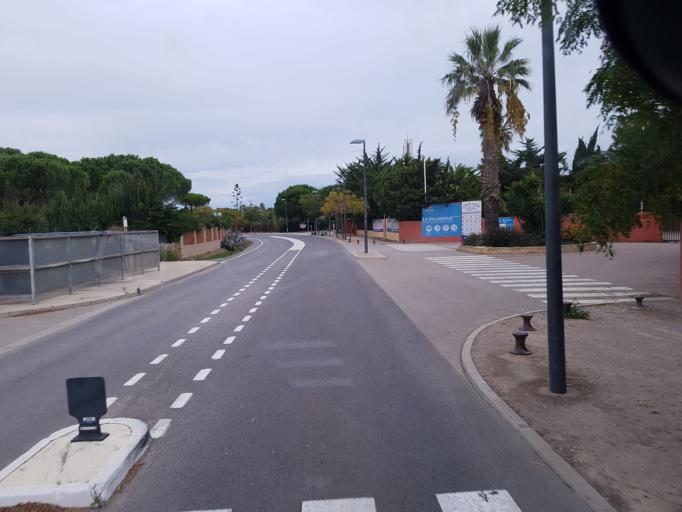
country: FR
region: Languedoc-Roussillon
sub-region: Departement des Pyrenees-Orientales
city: Le Barcares
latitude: 42.7656
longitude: 3.0270
